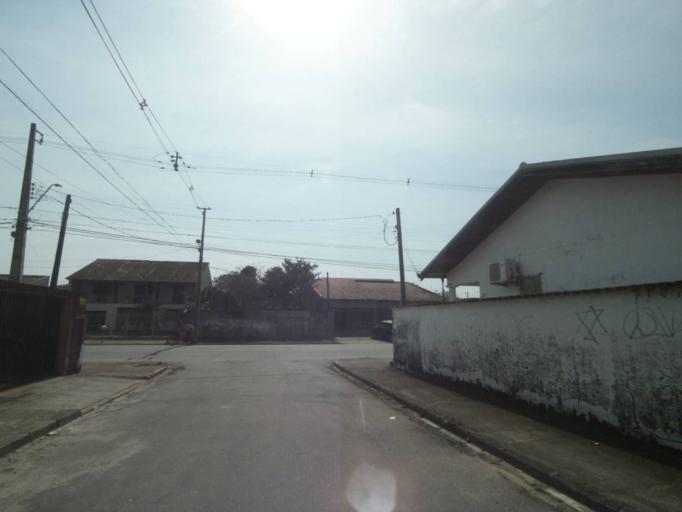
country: BR
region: Parana
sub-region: Paranagua
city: Paranagua
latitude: -25.5226
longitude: -48.5241
